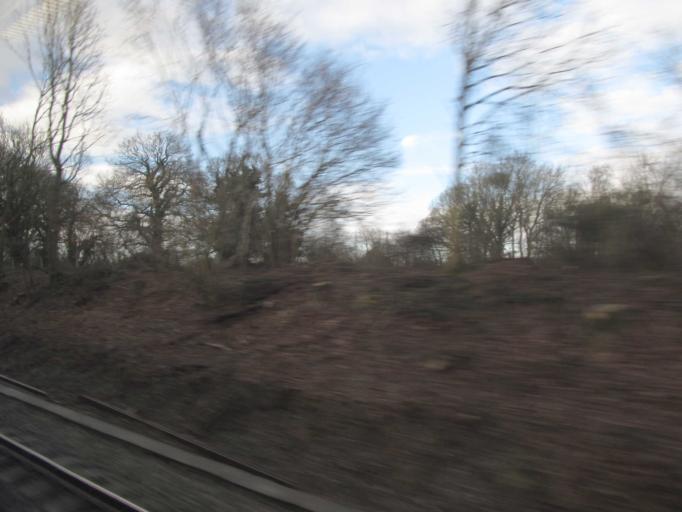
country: GB
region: England
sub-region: West Berkshire
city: Stratfield Mortimer
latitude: 51.3391
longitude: -1.0622
